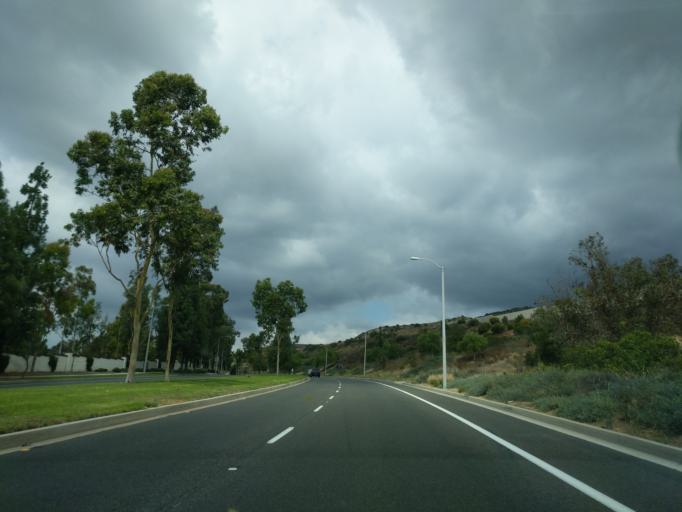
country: US
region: California
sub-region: Orange County
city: North Tustin
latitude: 33.7620
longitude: -117.7611
